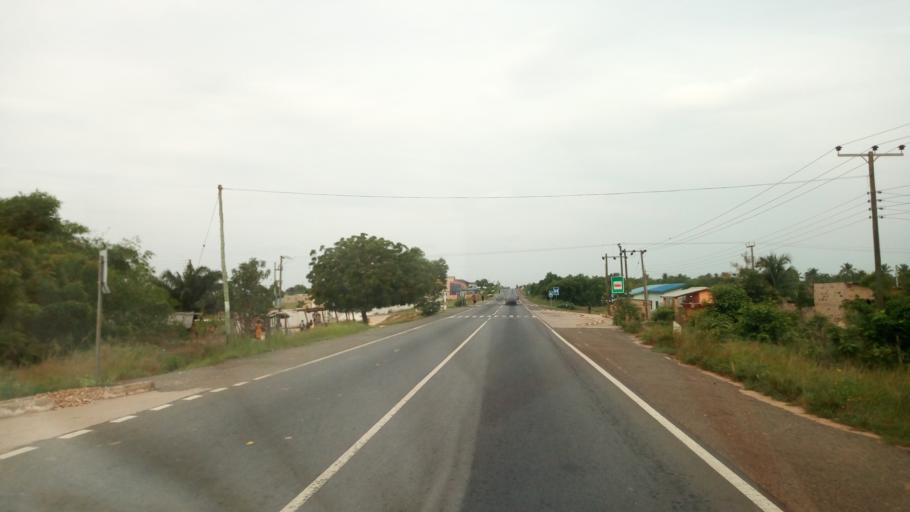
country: GH
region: Volta
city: Keta
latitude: 6.0587
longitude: 0.9926
